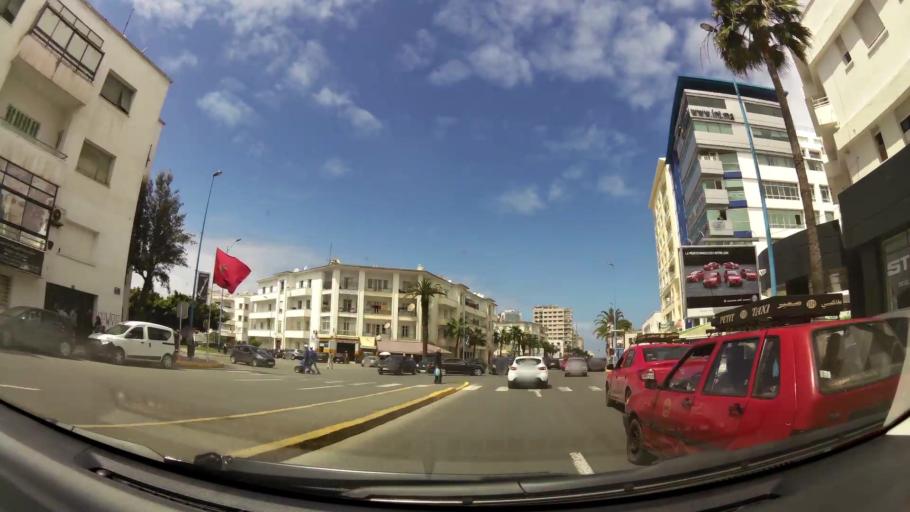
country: MA
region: Grand Casablanca
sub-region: Casablanca
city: Casablanca
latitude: 33.5937
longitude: -7.6376
